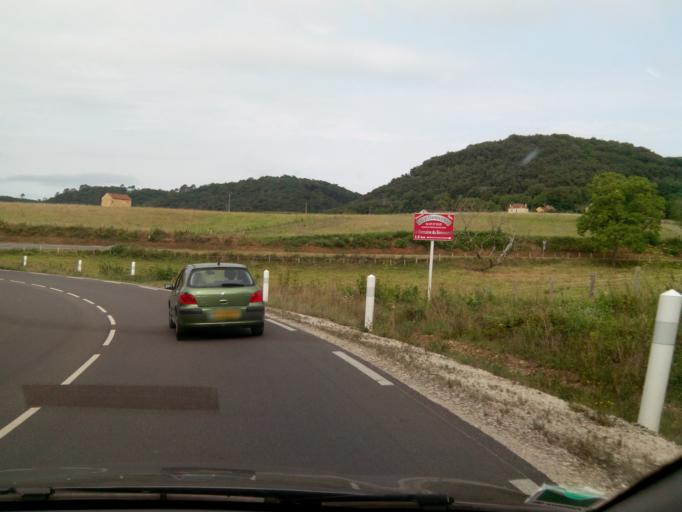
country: FR
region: Aquitaine
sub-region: Departement de la Dordogne
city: Eyvigues-et-Eybenes
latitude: 44.8596
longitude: 1.3453
